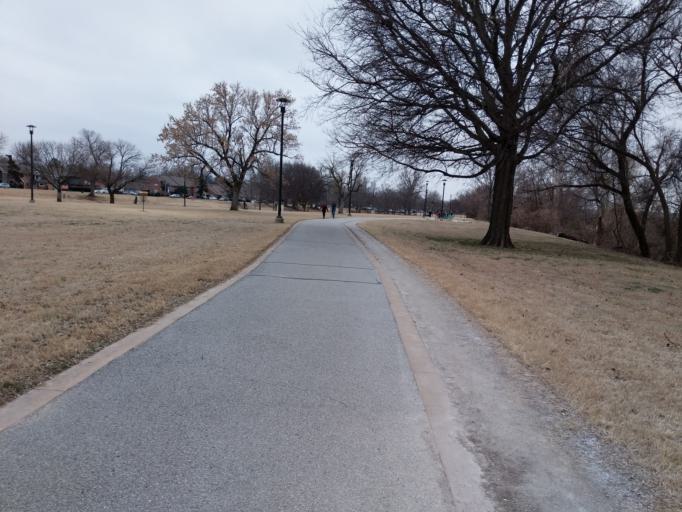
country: US
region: Oklahoma
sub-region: Tulsa County
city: Tulsa
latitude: 36.1080
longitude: -95.9842
